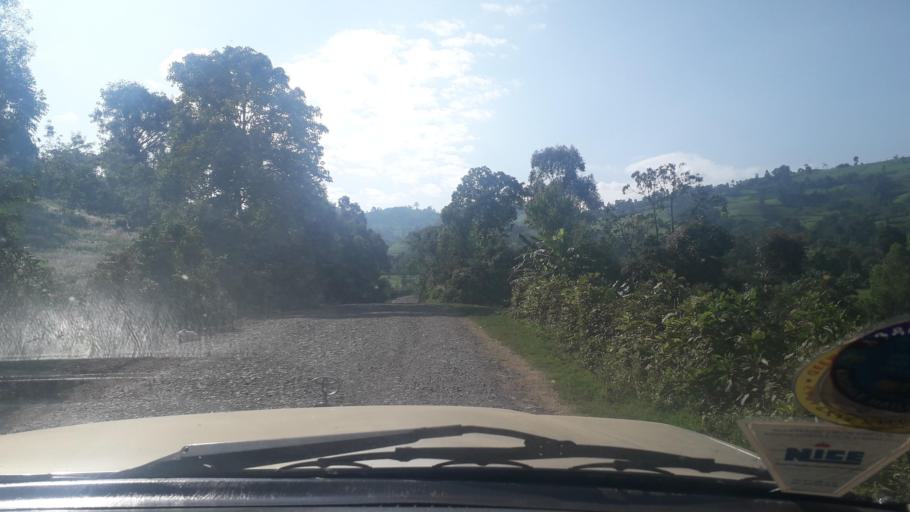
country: ET
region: Oromiya
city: Jima
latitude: 7.3852
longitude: 36.8662
